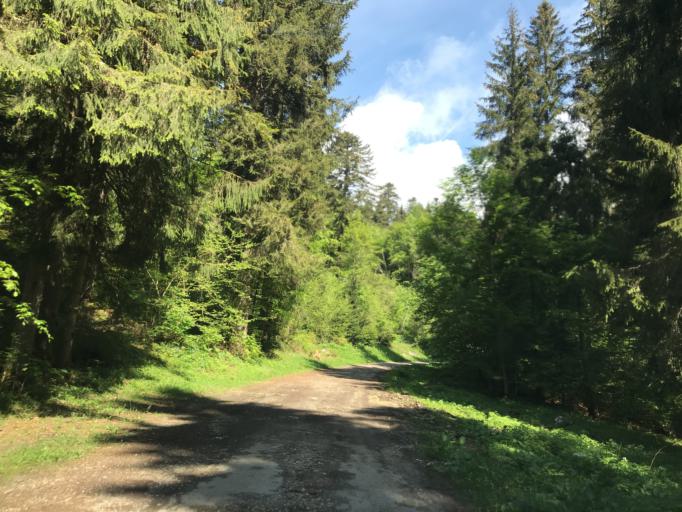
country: FR
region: Rhone-Alpes
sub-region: Departement de la Savoie
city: La Motte-Servolex
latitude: 45.5876
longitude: 5.8214
